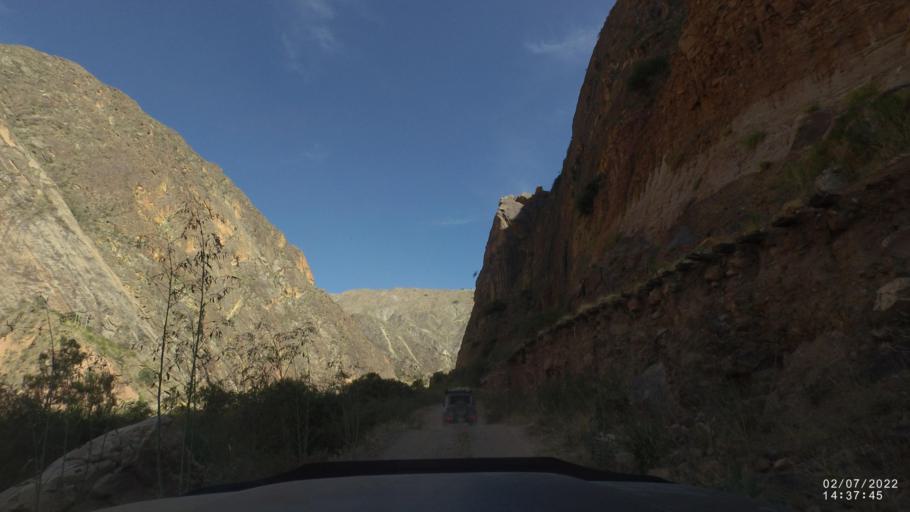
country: BO
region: Cochabamba
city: Irpa Irpa
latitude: -17.8426
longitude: -66.4188
